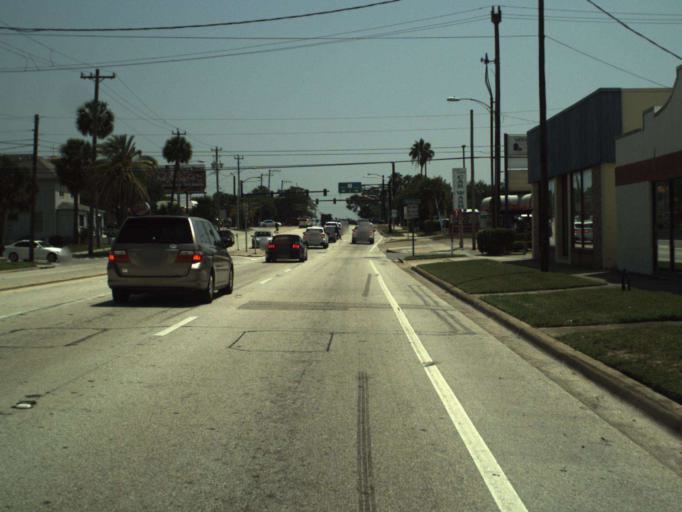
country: US
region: Florida
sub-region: Volusia County
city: Daytona Beach
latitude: 29.2100
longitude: -81.0247
